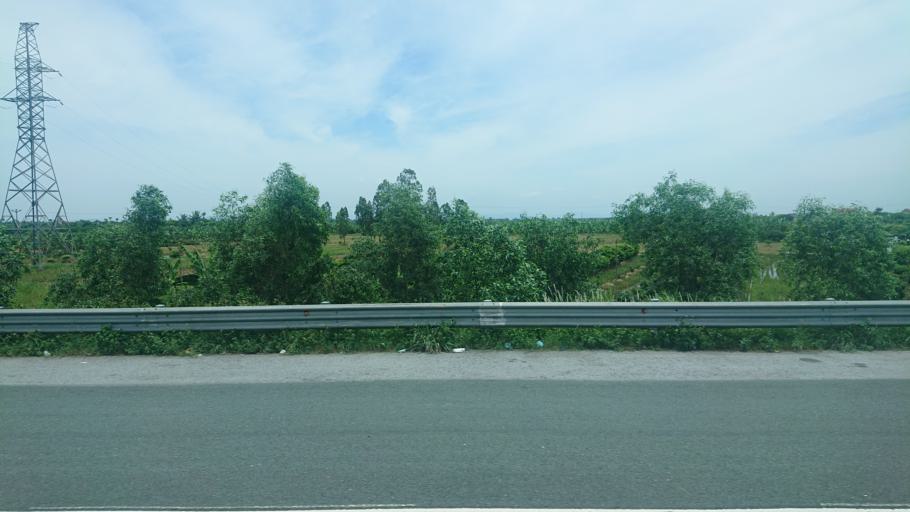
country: VN
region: Hai Phong
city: An Lao
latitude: 20.8136
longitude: 106.4978
